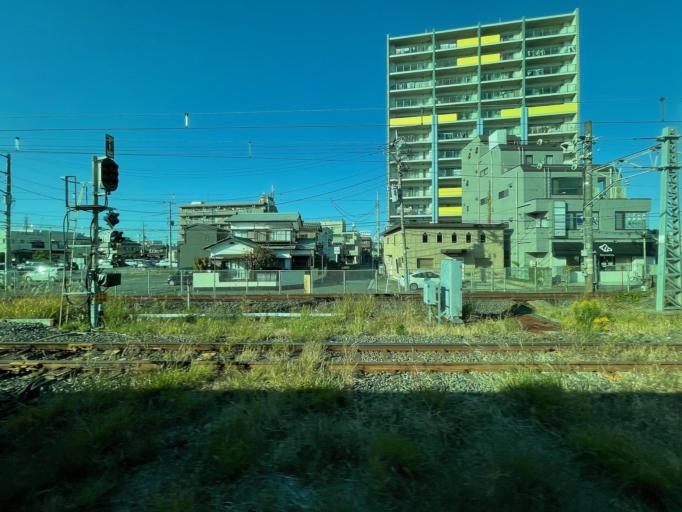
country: JP
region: Chiba
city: Sakura
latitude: 35.7096
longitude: 140.2249
